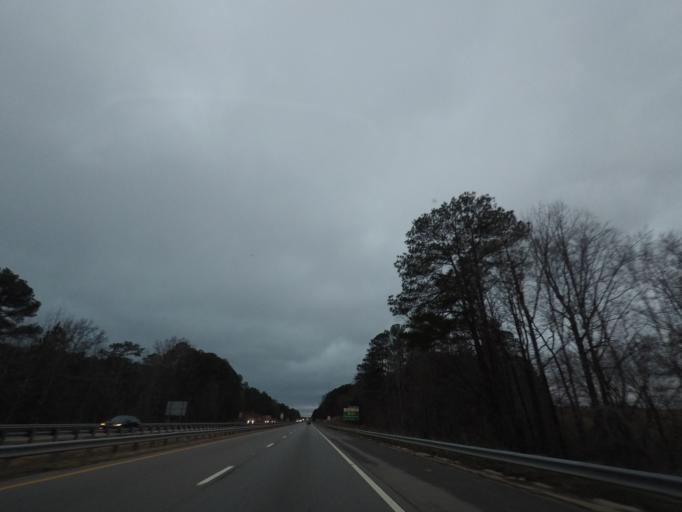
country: US
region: North Carolina
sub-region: Wake County
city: Apex
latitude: 35.7095
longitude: -78.8470
